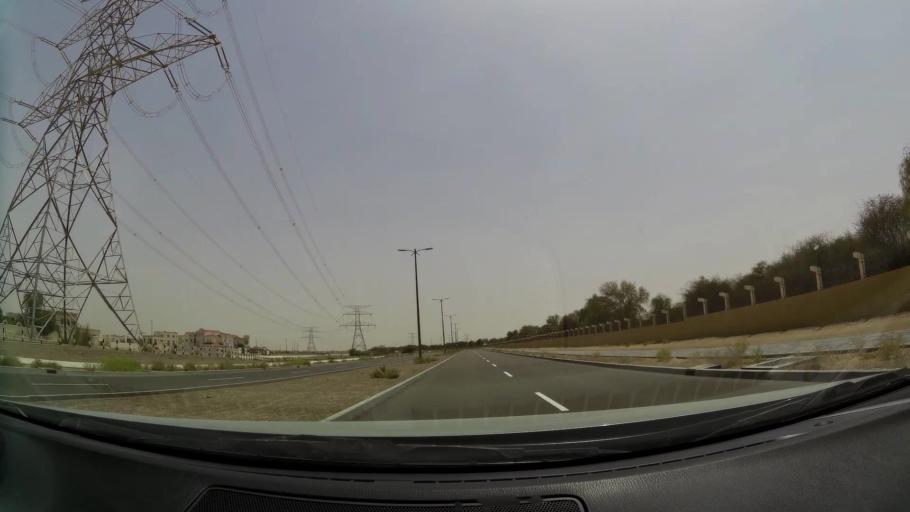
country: AE
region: Abu Dhabi
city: Al Ain
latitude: 24.1692
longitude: 55.6572
